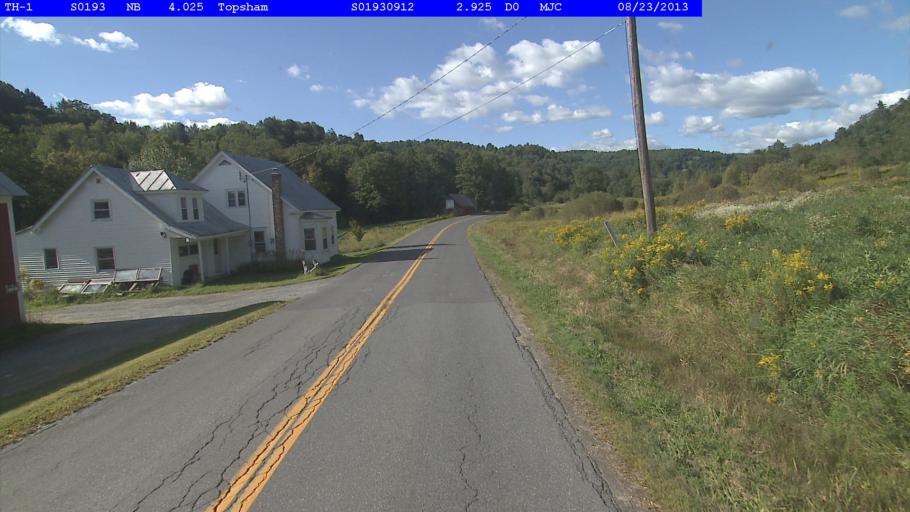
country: US
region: New Hampshire
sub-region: Grafton County
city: Haverhill
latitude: 44.1095
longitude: -72.2335
